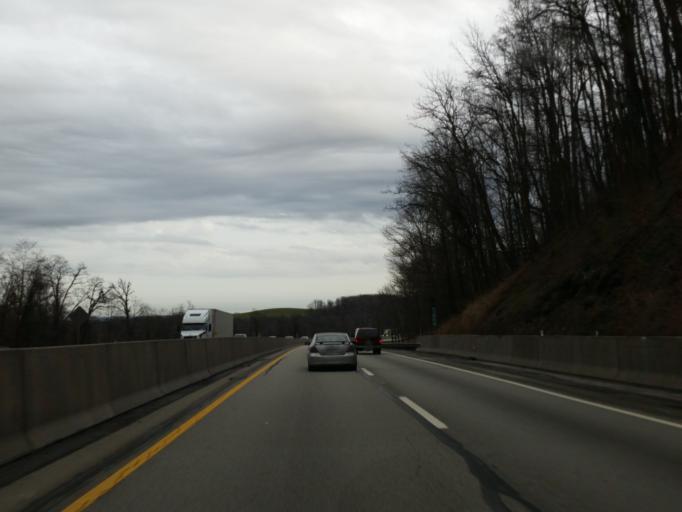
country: US
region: Pennsylvania
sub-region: Somerset County
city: Somerset
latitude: 40.0534
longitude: -79.1278
